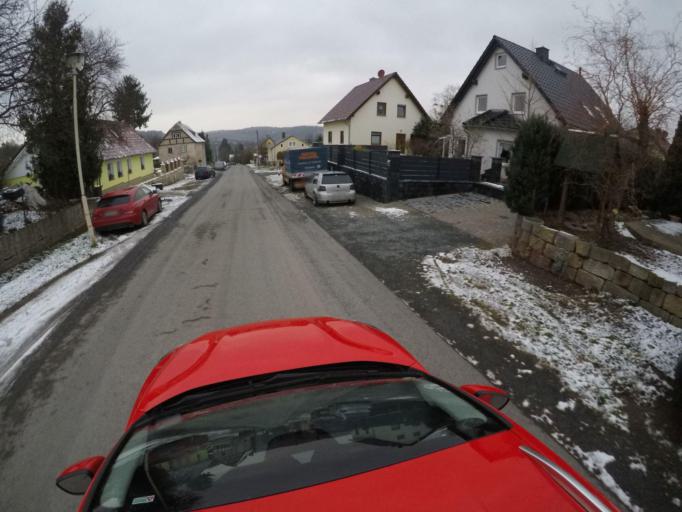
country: DE
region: Saxony
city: Dohma
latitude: 50.8713
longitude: 13.9534
